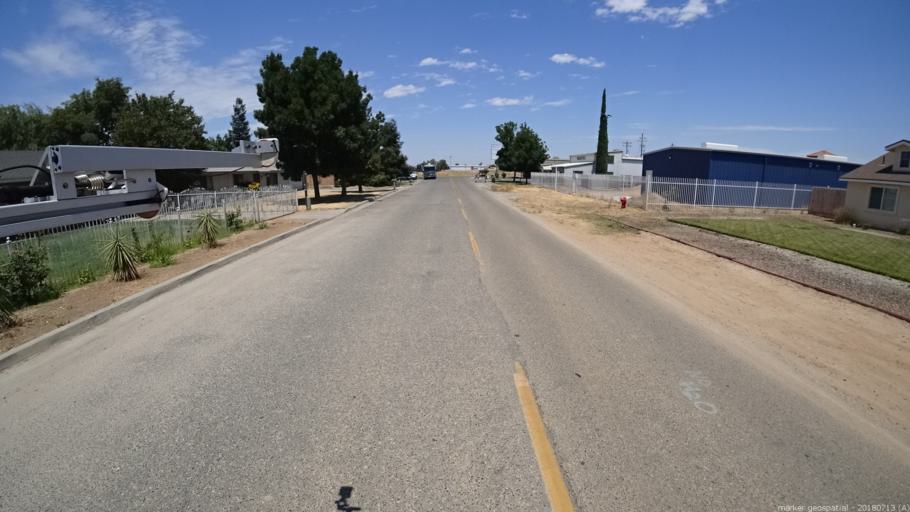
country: US
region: California
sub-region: Madera County
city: Madera Acres
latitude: 36.9952
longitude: -120.0754
